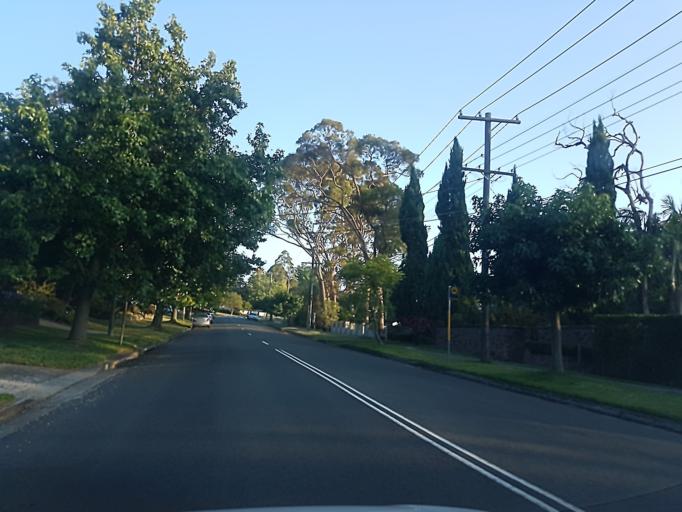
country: AU
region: New South Wales
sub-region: Warringah
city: Davidson
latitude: -33.7443
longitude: 151.2078
